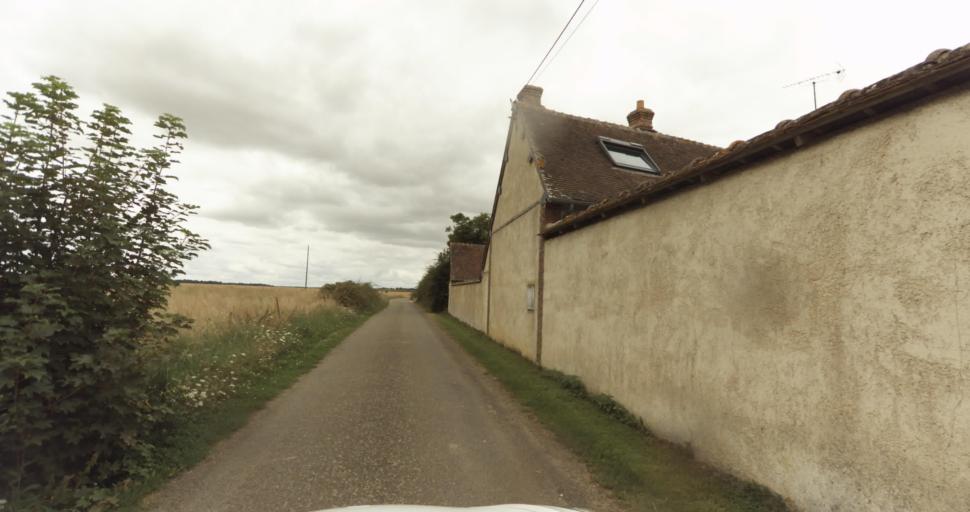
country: FR
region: Haute-Normandie
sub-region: Departement de l'Eure
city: Nonancourt
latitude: 48.8005
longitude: 1.1601
